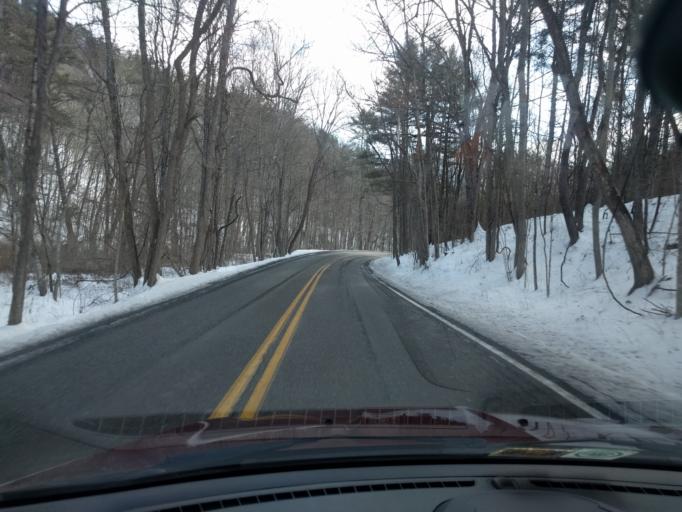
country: US
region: Virginia
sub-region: Bath County
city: Warm Springs
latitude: 38.1245
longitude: -79.9249
